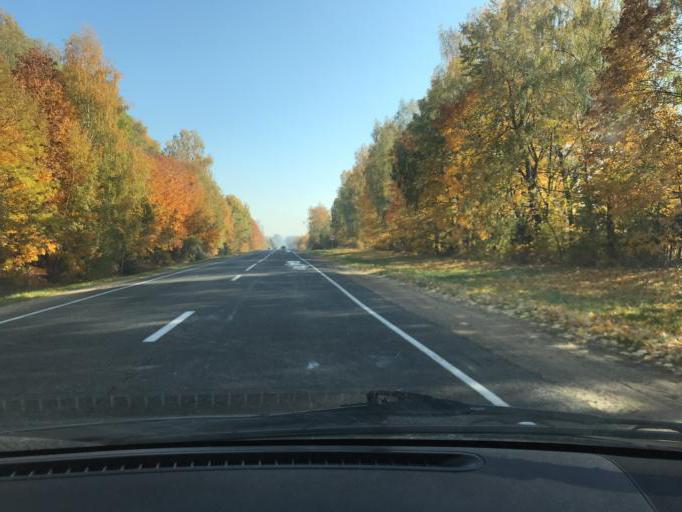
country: BY
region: Brest
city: Lyakhavichy
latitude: 52.9568
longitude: 26.3178
